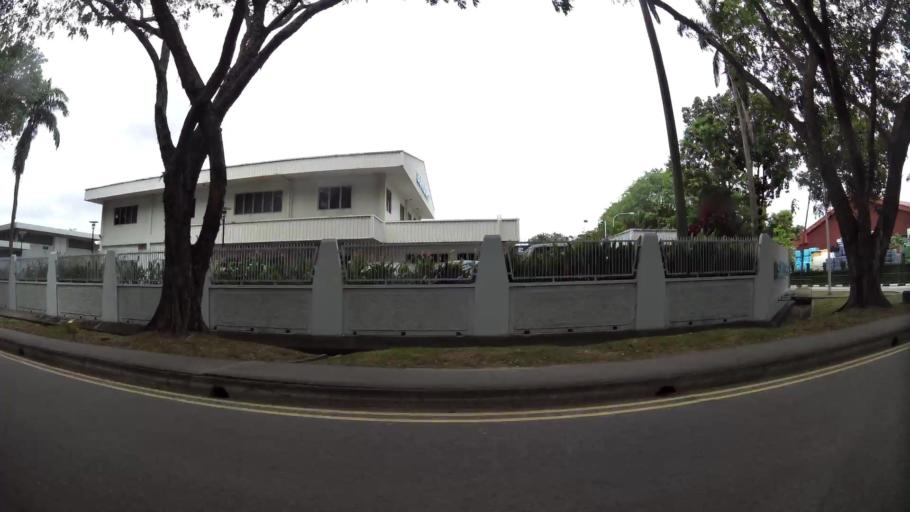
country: SG
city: Singapore
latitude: 1.3304
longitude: 103.7165
